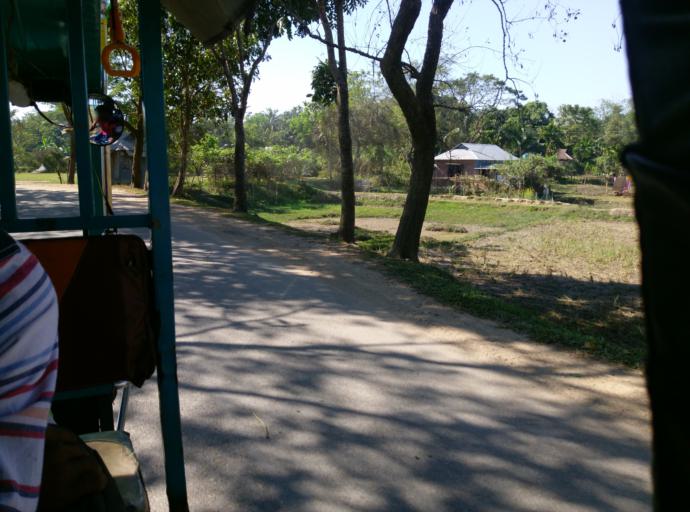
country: BD
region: Dhaka
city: Netrakona
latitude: 25.0658
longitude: 90.4993
